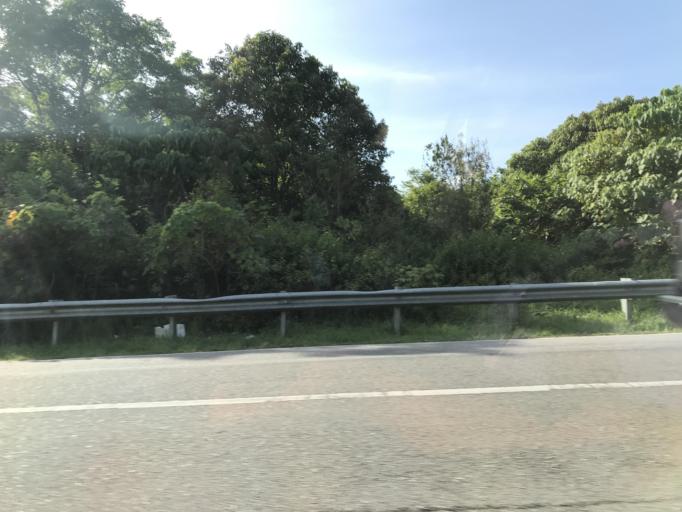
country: MY
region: Kelantan
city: Peringat
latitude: 6.0559
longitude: 102.2274
